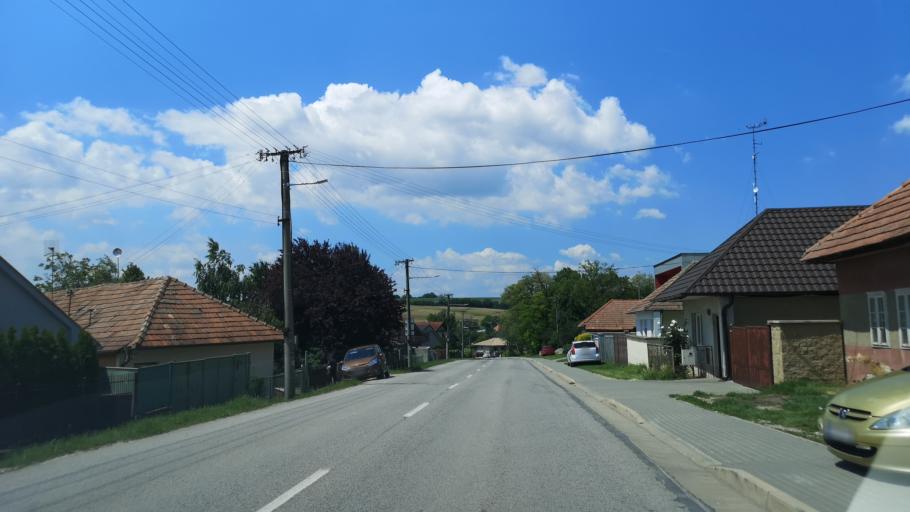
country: SK
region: Nitriansky
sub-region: Okres Nitra
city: Nitra
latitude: 48.3086
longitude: 17.9336
